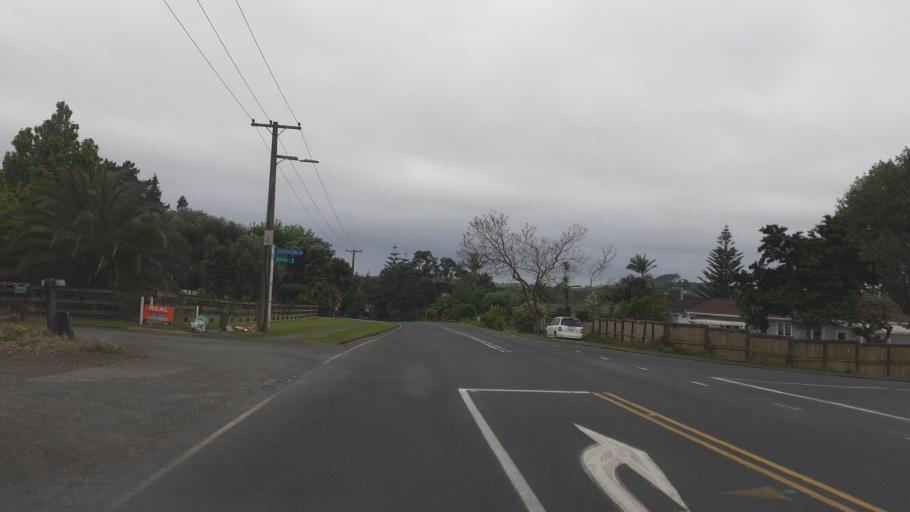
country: NZ
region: Northland
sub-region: Far North District
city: Kerikeri
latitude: -35.2068
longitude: 173.9653
